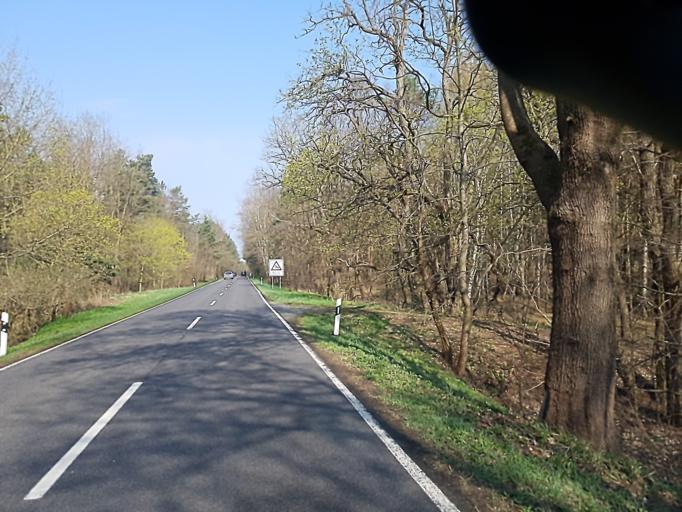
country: DE
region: Saxony-Anhalt
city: Radis
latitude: 51.6958
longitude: 12.5168
